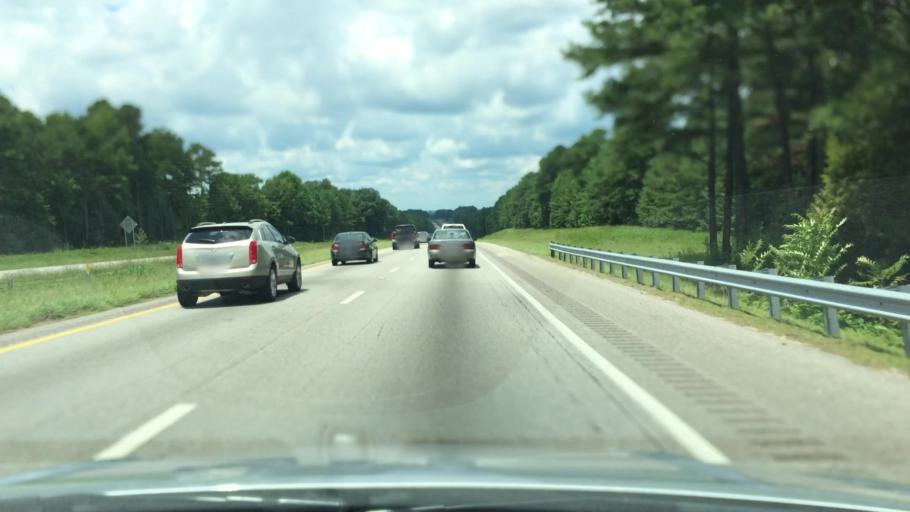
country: US
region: South Carolina
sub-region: Laurens County
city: Joanna
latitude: 34.4684
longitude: -81.8057
